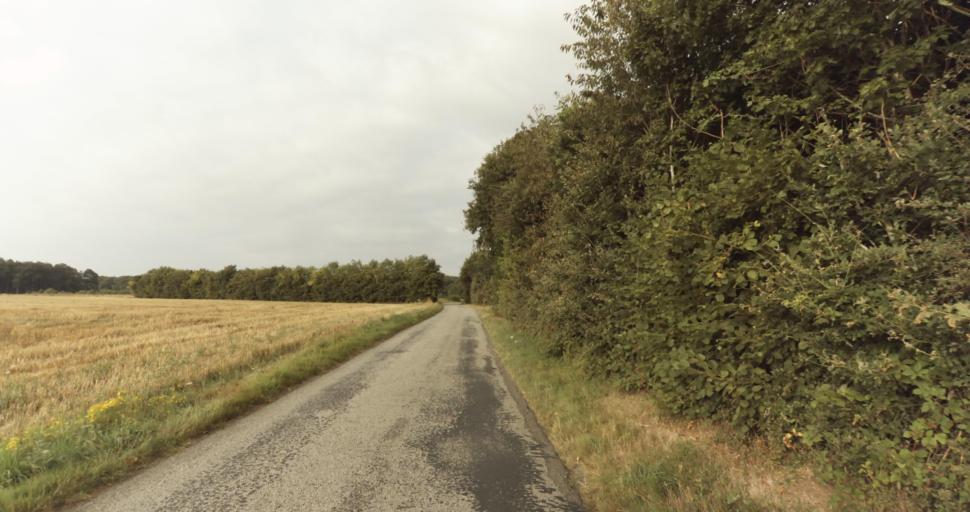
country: FR
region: Centre
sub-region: Departement d'Eure-et-Loir
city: Vert-en-Drouais
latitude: 48.7780
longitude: 1.3124
